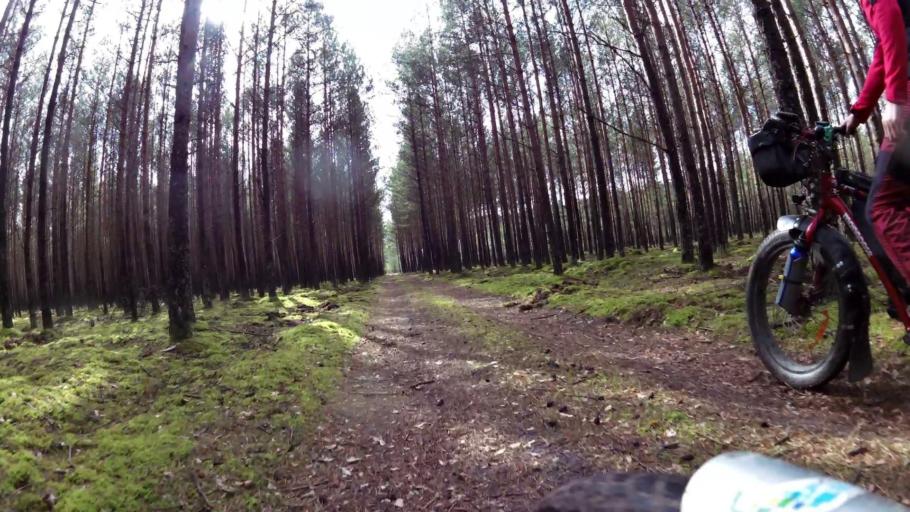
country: PL
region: Pomeranian Voivodeship
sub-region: Powiat bytowski
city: Kolczyglowy
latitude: 54.1876
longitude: 17.2121
